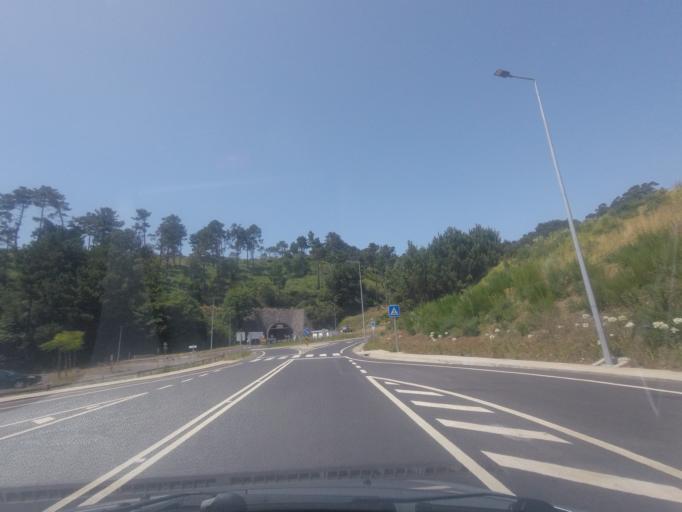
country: PT
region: Madeira
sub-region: Calheta
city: Faja da Ovelha
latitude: 32.7764
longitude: -17.2197
